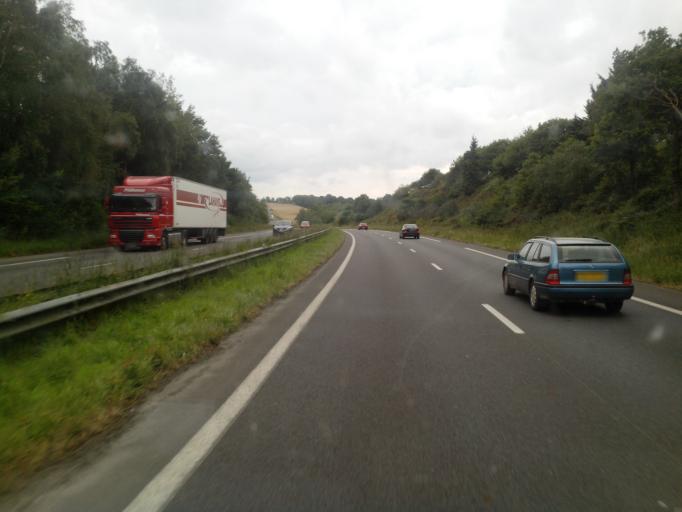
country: FR
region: Brittany
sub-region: Departement des Cotes-d'Armor
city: Coetmieux
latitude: 48.4733
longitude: -2.5596
